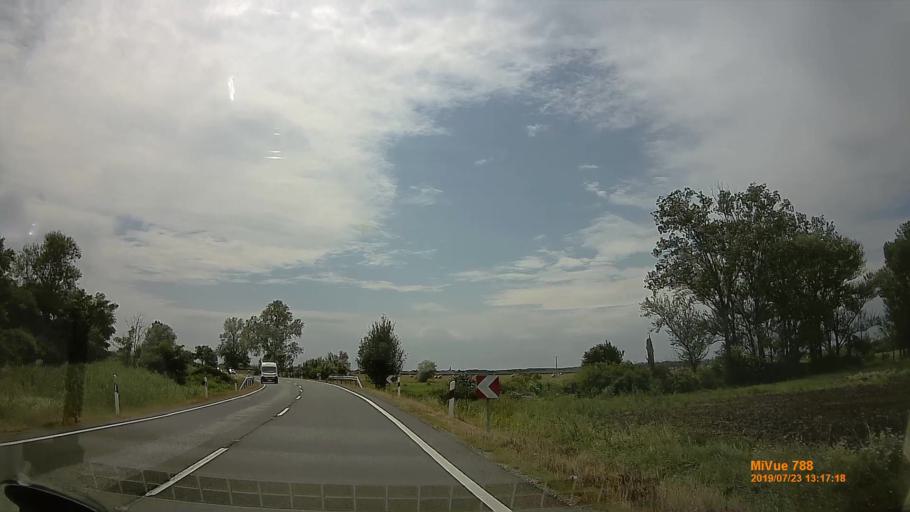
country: HU
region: Hajdu-Bihar
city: Polgar
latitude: 47.9007
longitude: 21.1585
